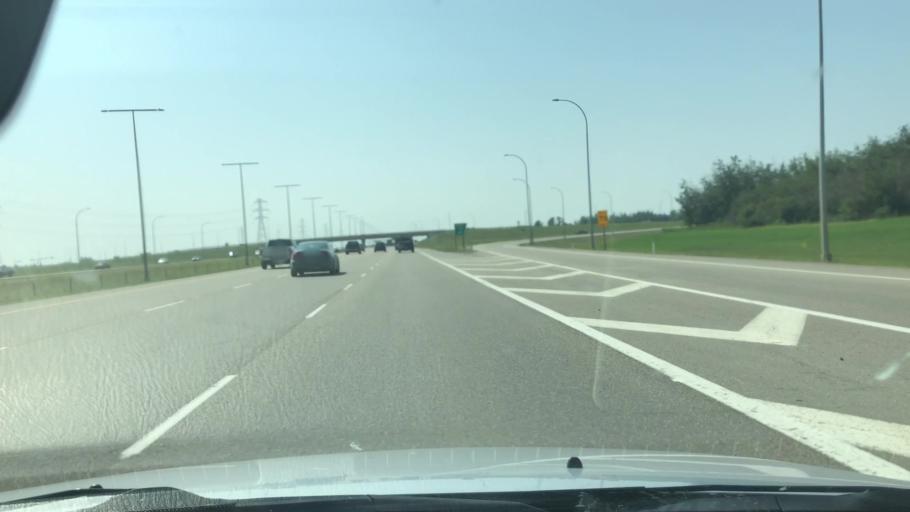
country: CA
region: Alberta
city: St. Albert
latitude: 53.5282
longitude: -113.6598
